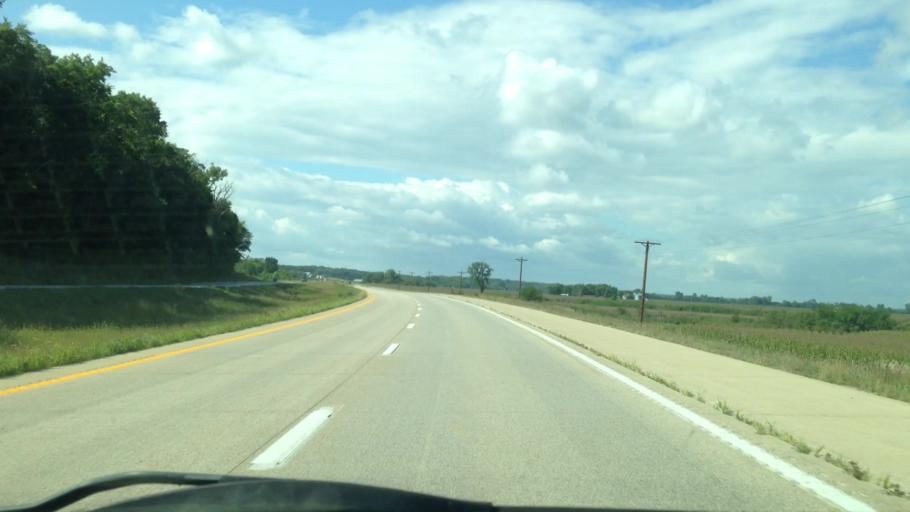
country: US
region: Illinois
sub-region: Hancock County
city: Warsaw
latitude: 40.3164
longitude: -91.5763
